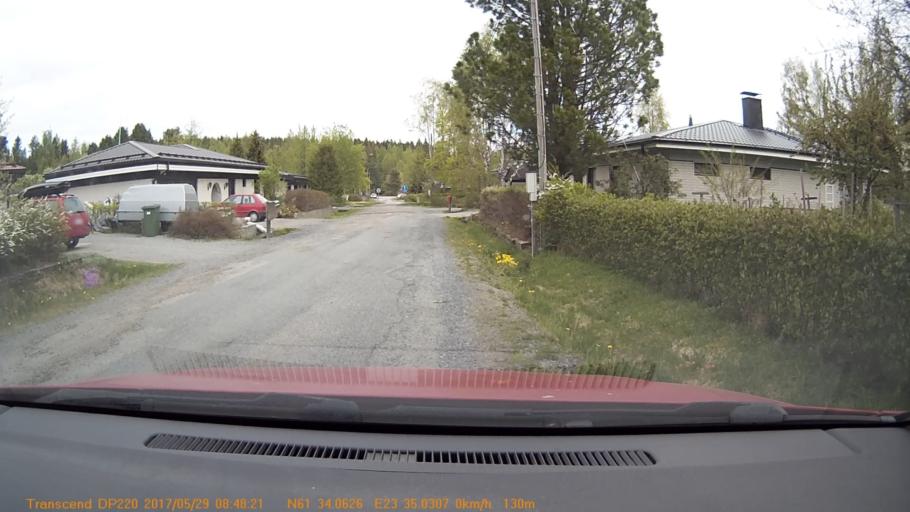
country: FI
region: Pirkanmaa
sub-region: Tampere
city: Yloejaervi
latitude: 61.5677
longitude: 23.5840
